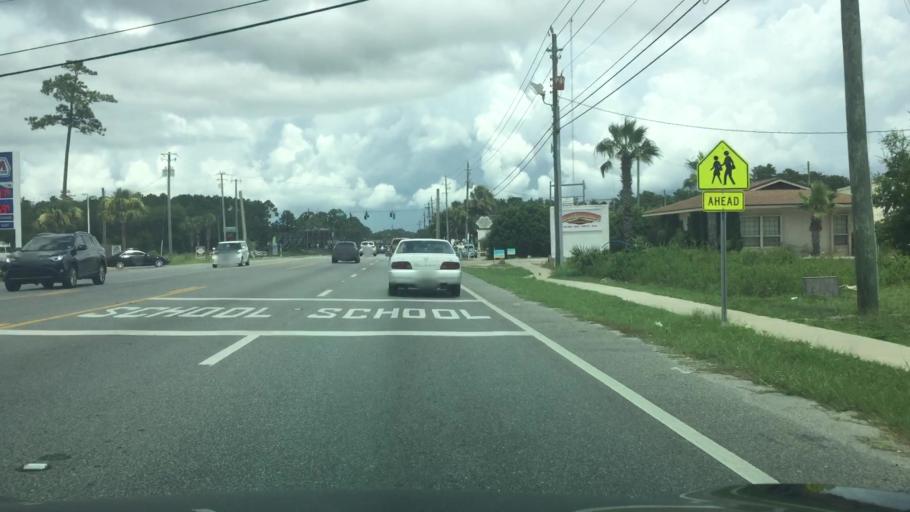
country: US
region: Florida
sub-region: Bay County
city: Upper Grand Lagoon
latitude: 30.1672
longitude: -85.7570
